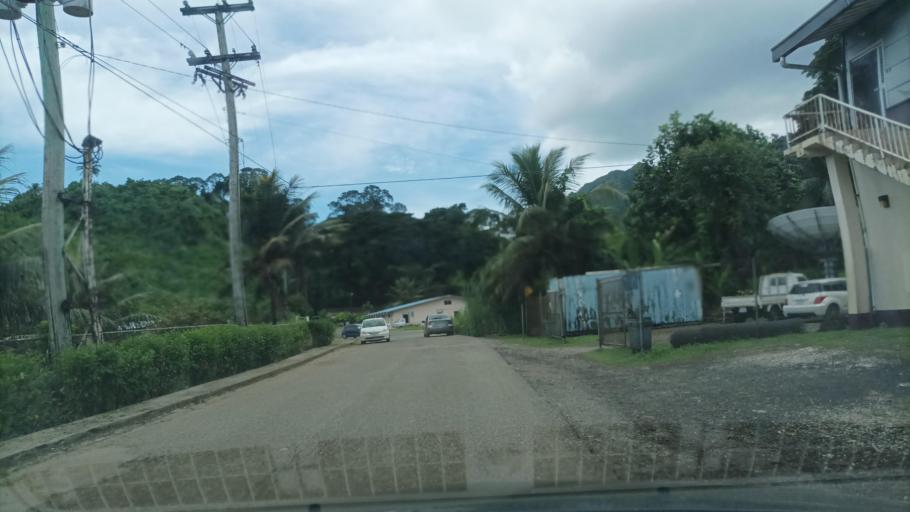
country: FM
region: Kosrae
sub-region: Lelu Municipality
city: Tofol
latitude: 5.3264
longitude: 163.0085
